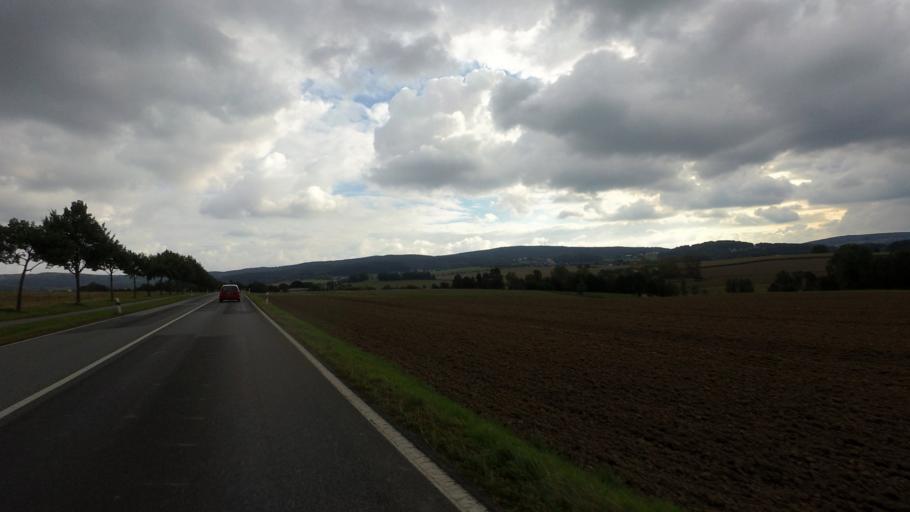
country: DE
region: Saxony
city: Crostau
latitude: 51.1039
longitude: 14.4612
